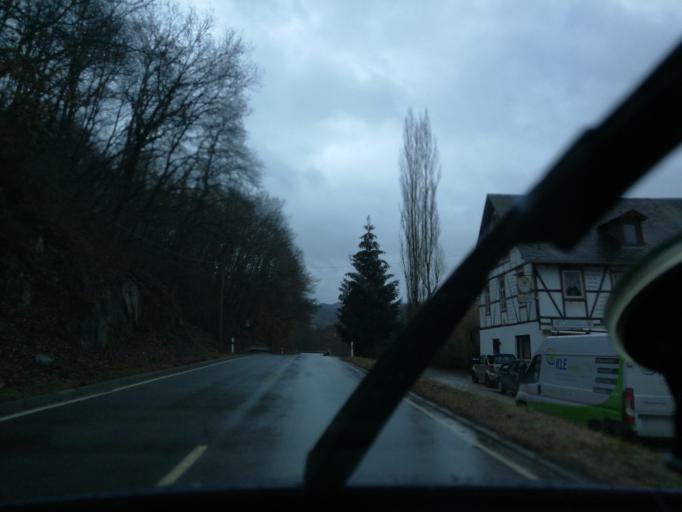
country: DE
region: Rheinland-Pfalz
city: Minheim
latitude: 49.8419
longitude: 6.9302
